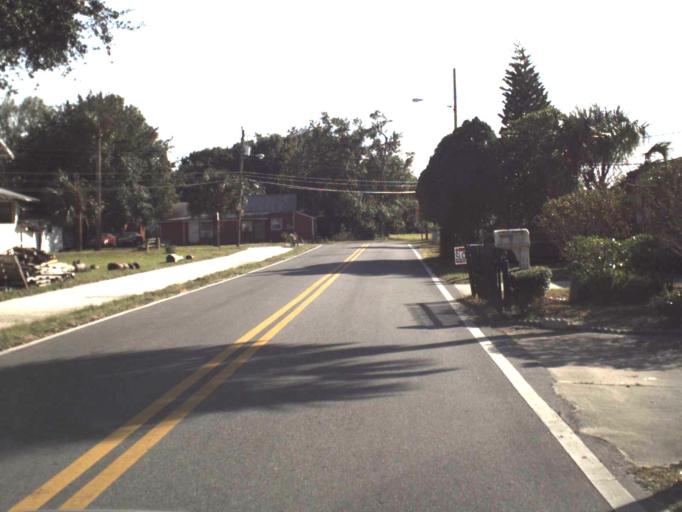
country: US
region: Florida
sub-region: Seminole County
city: Sanford
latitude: 28.7996
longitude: -81.2889
